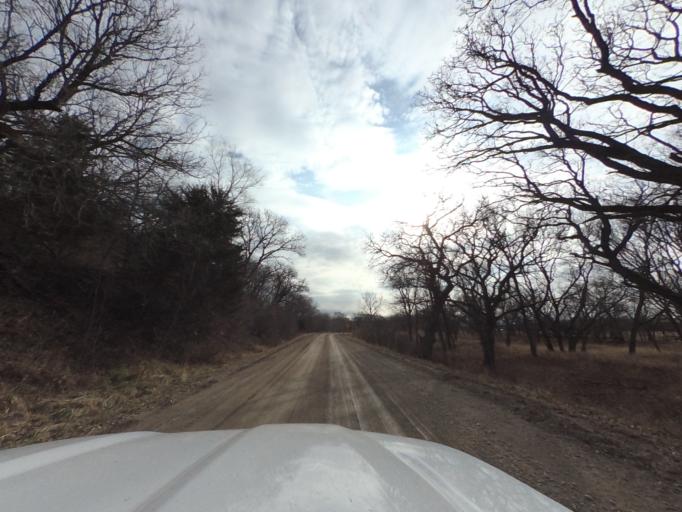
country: US
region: Kansas
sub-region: Chase County
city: Cottonwood Falls
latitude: 38.2761
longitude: -96.7335
